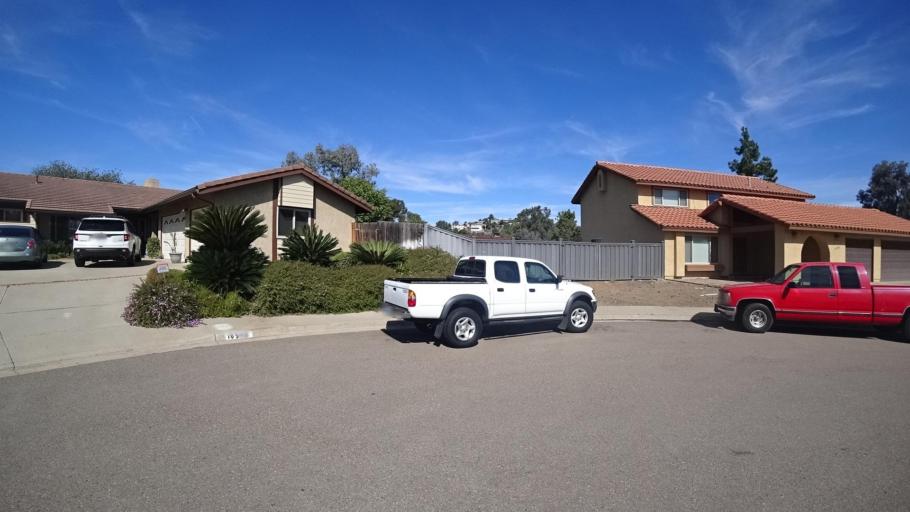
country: US
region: California
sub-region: San Diego County
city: Casa de Oro-Mount Helix
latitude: 32.7534
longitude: -116.9573
